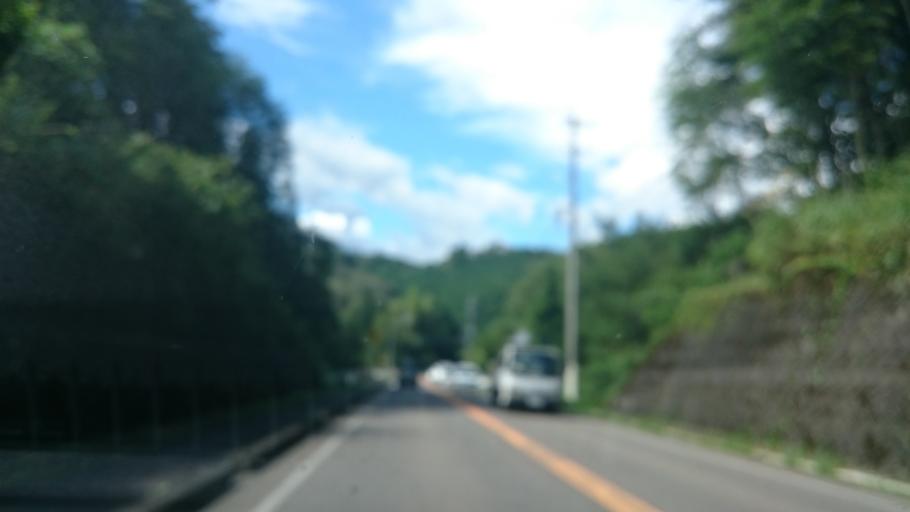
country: JP
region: Gifu
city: Nakatsugawa
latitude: 35.5942
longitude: 137.4618
